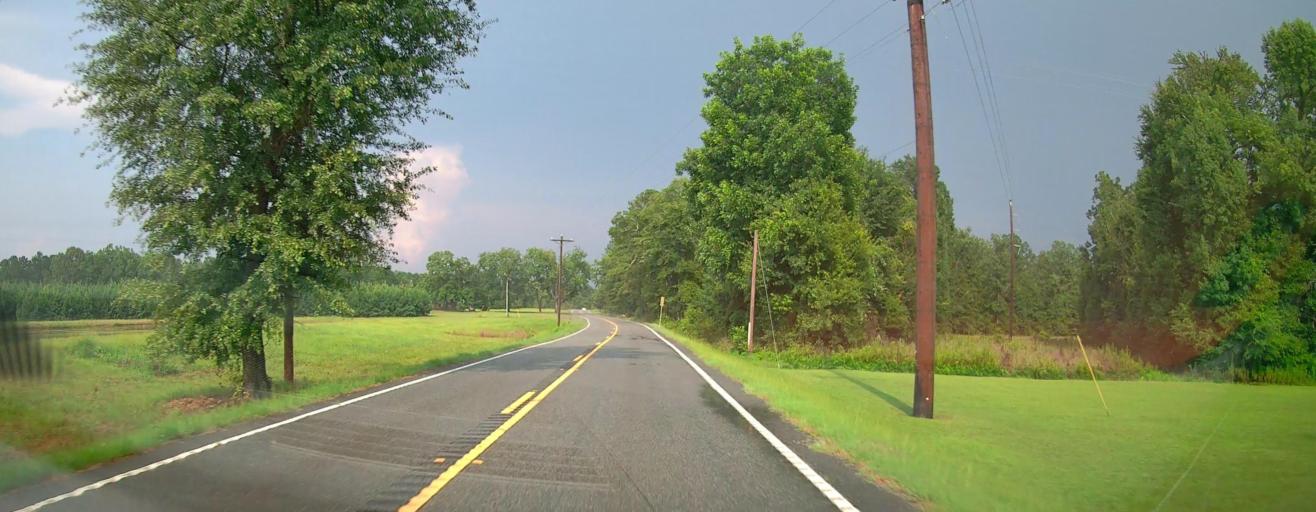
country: US
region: Georgia
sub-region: Twiggs County
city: Jeffersonville
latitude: 32.6048
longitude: -83.2883
